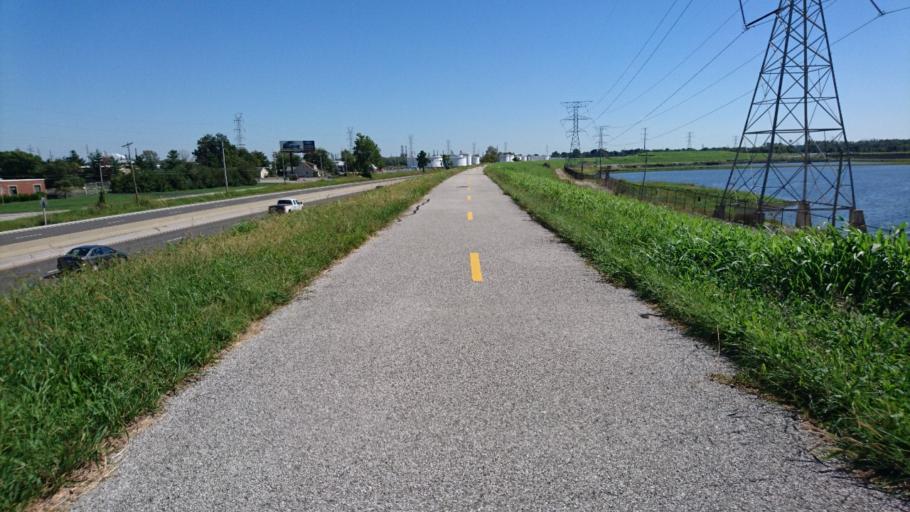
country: US
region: Illinois
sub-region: Madison County
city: Wood River
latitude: 38.8511
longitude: -90.1024
